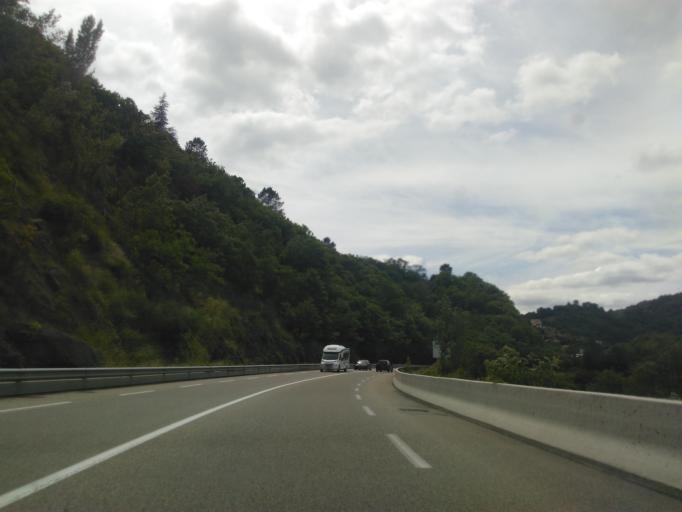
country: FR
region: Rhone-Alpes
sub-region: Departement de l'Ardeche
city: Labegude
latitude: 44.6473
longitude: 4.3607
